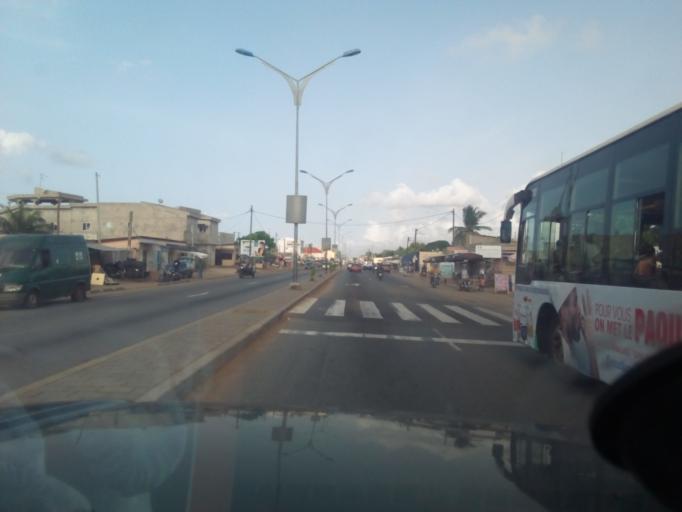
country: TG
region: Maritime
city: Lome
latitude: 6.1696
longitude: 1.3446
